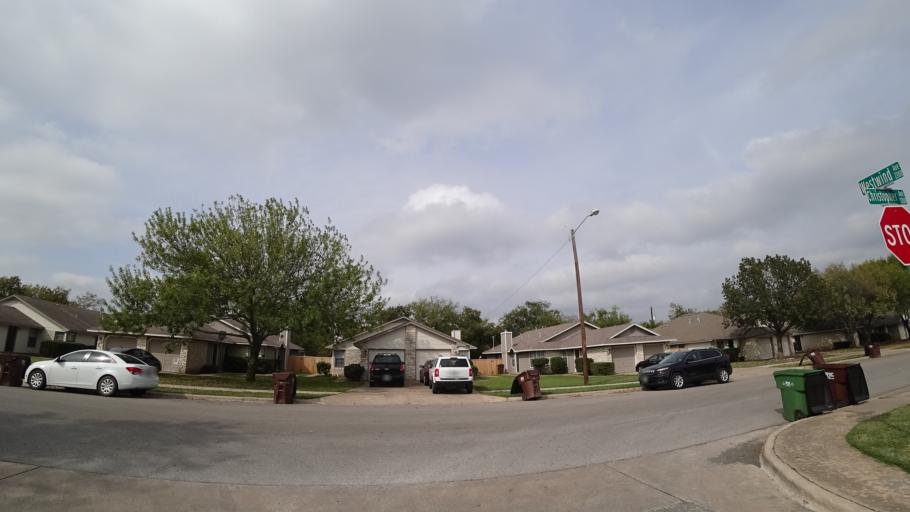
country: US
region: Texas
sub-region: Williamson County
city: Round Rock
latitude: 30.4911
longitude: -97.6938
